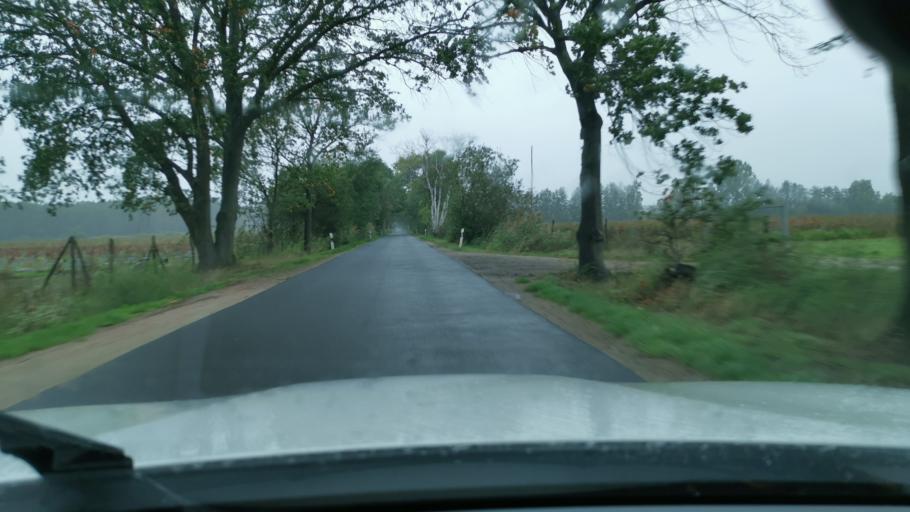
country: DE
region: Brandenburg
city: Borkheide
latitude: 52.2009
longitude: 12.9039
